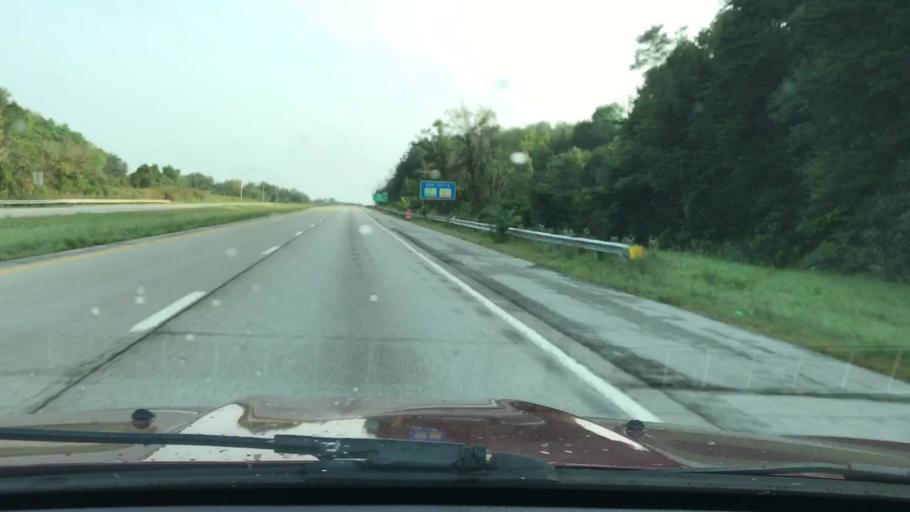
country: US
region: Ohio
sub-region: Washington County
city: Devola
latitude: 39.4740
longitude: -81.4389
